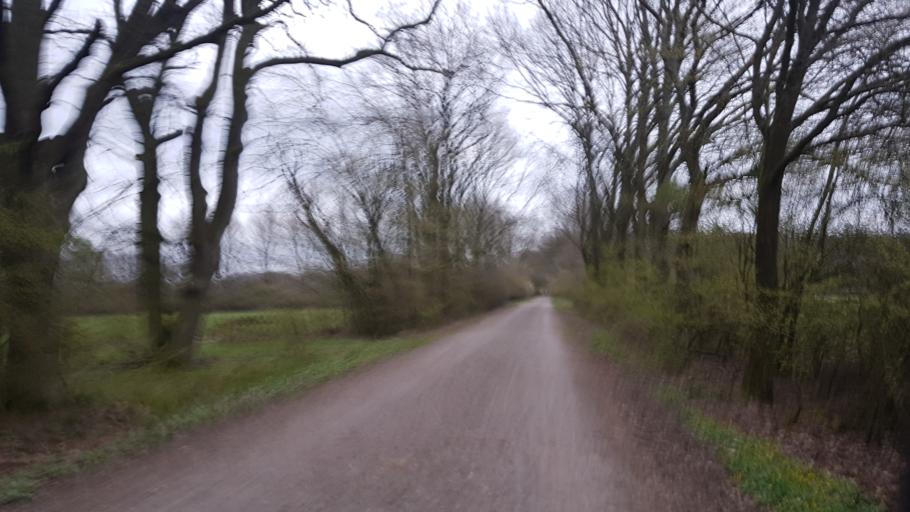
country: DE
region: Lower Saxony
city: Isernhagen Farster Bauerschaft
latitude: 52.4457
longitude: 9.8096
